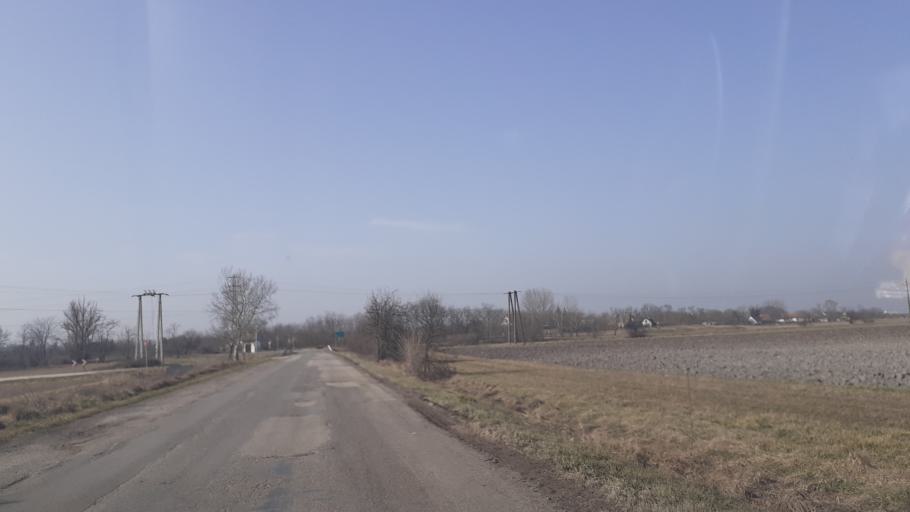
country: HU
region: Pest
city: Dabas
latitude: 47.0671
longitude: 19.2595
